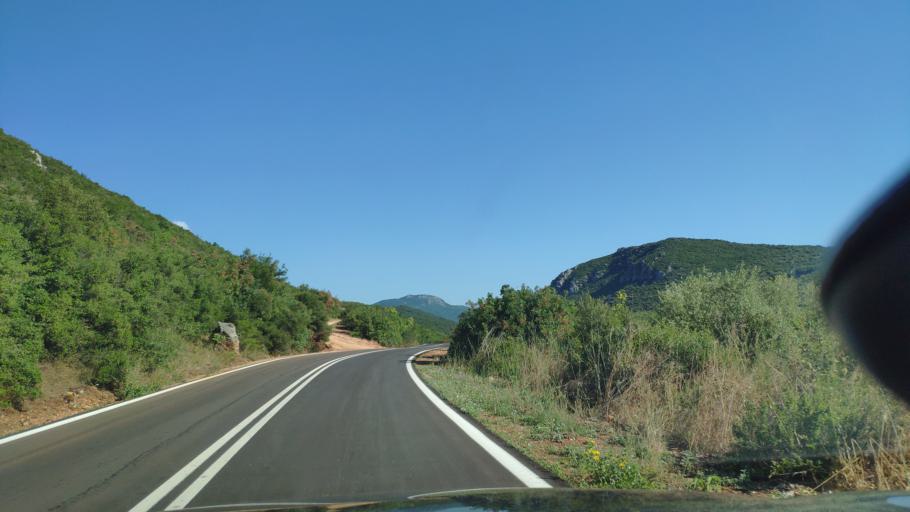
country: GR
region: West Greece
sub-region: Nomos Aitolias kai Akarnanias
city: Fitiai
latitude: 38.6684
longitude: 21.1418
